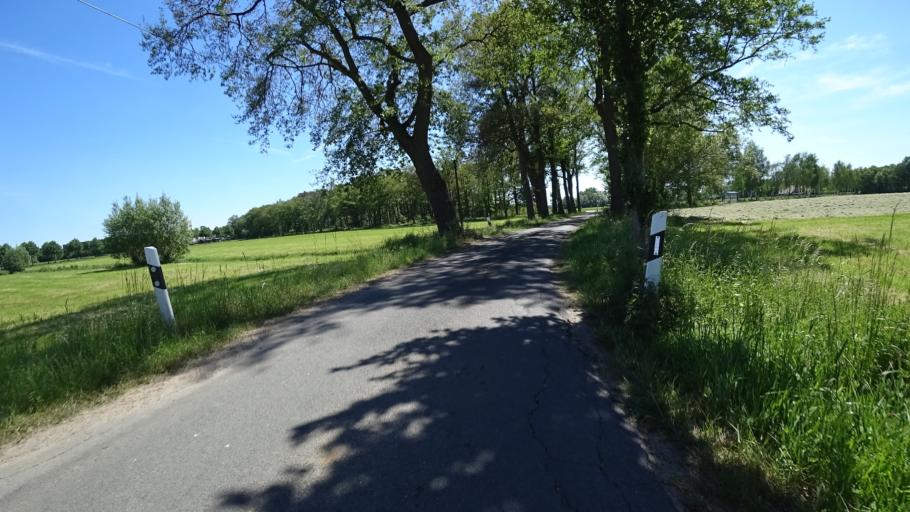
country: DE
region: North Rhine-Westphalia
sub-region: Regierungsbezirk Detmold
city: Guetersloh
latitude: 51.8585
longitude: 8.3624
